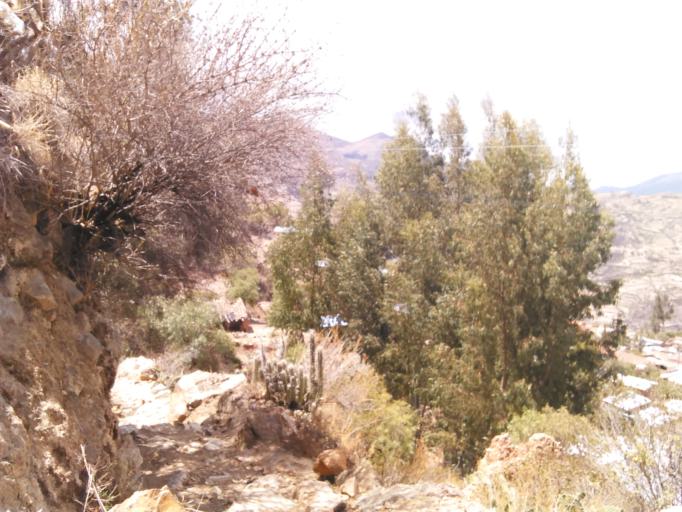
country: PE
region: Ayacucho
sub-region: Provincia de Victor Fajardo
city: Canaria
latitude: -13.8810
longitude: -73.9334
